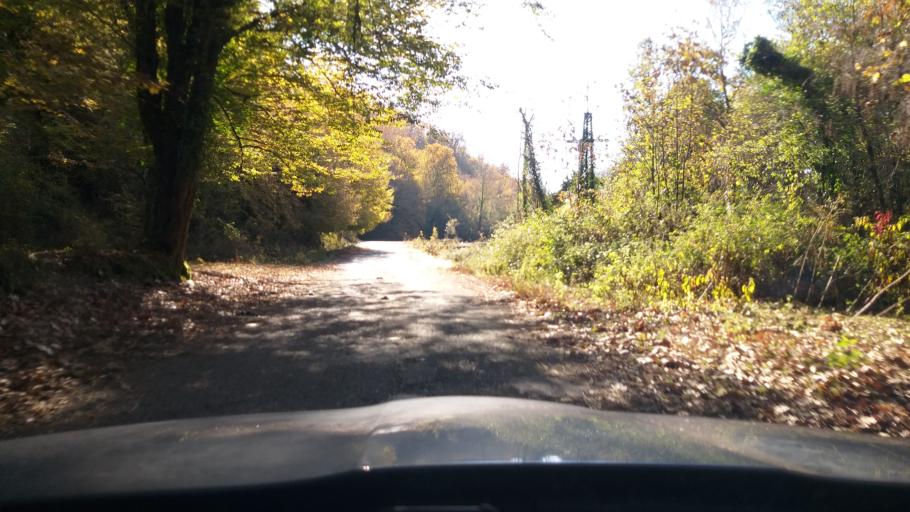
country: GE
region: Abkhazia
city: Bich'vinta
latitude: 43.1645
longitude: 40.4627
